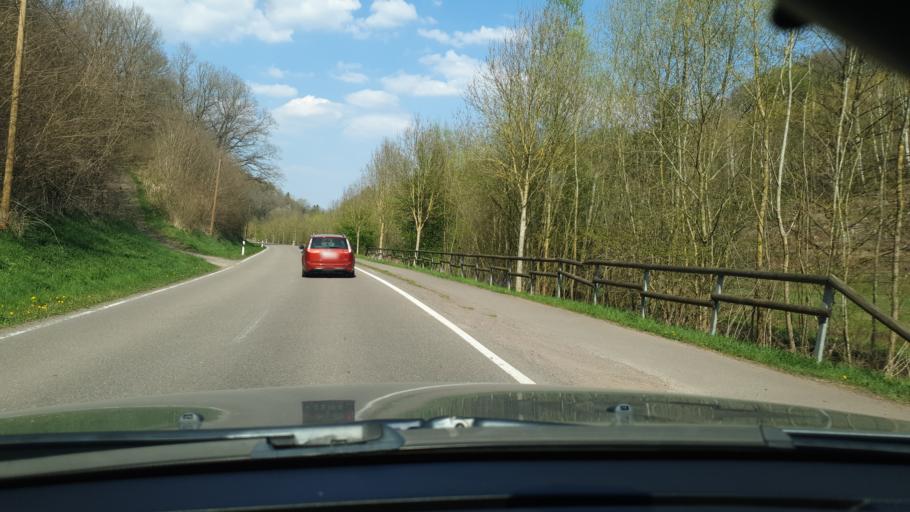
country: DE
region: Rheinland-Pfalz
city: Contwig
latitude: 49.2615
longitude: 7.4012
